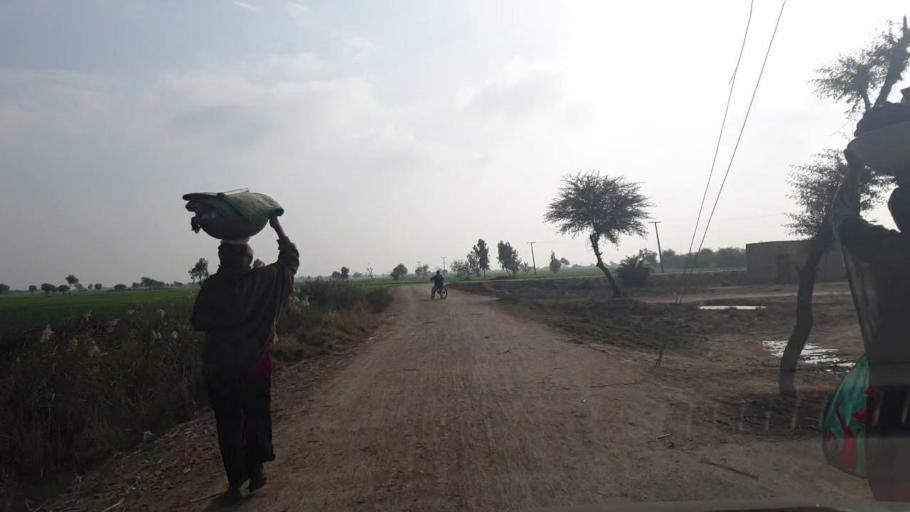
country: PK
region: Sindh
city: Shahdadpur
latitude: 25.8726
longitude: 68.6647
